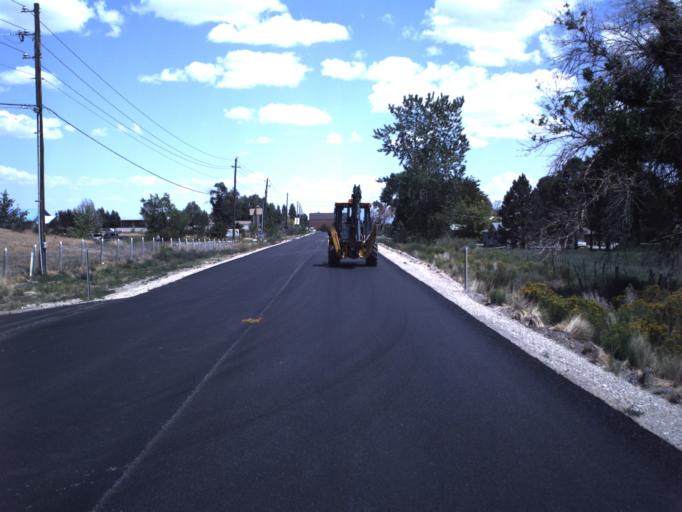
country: US
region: Utah
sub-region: Emery County
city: Castle Dale
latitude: 39.2279
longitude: -111.0311
